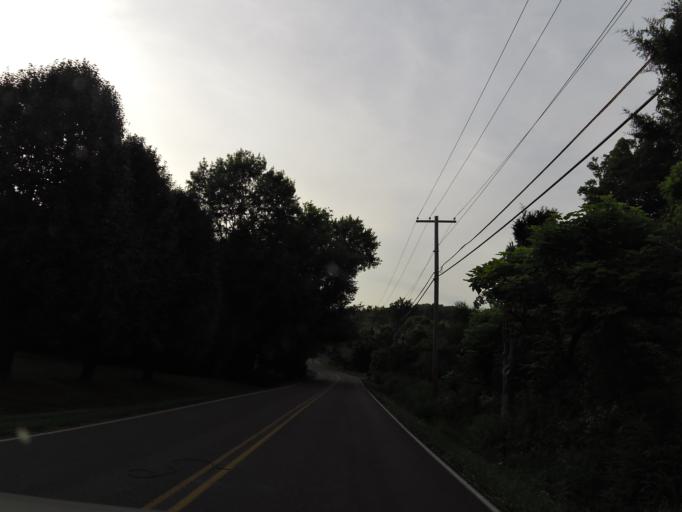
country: US
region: Tennessee
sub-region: Sevier County
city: Seymour
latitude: 35.8960
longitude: -83.7971
